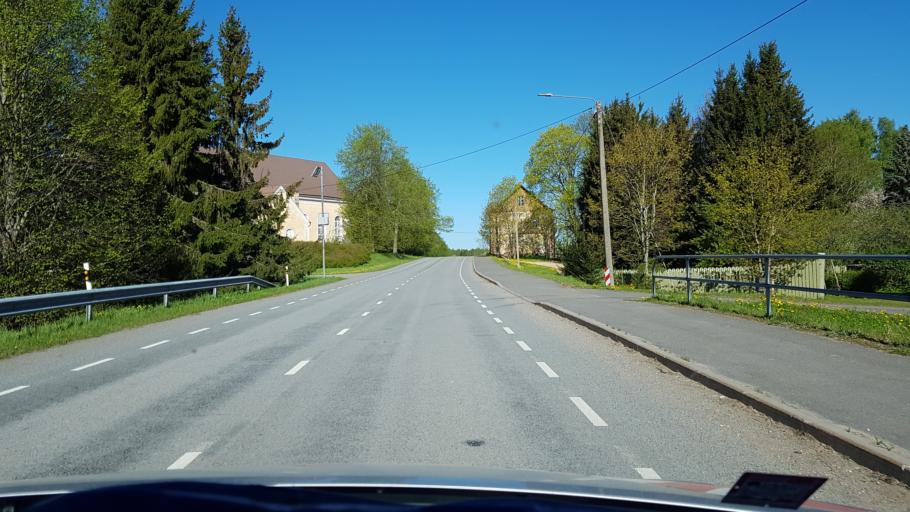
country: EE
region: Polvamaa
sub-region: Polva linn
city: Polva
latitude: 58.2839
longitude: 27.0442
